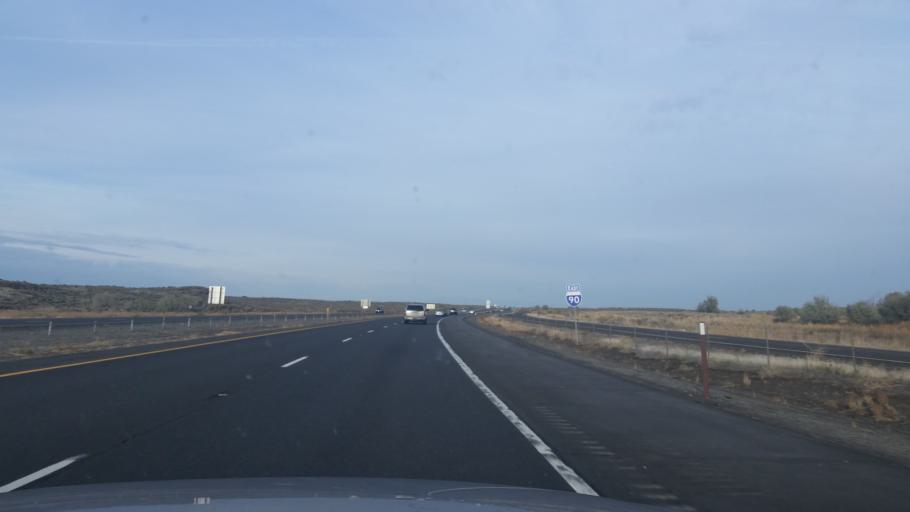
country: US
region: Washington
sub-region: Grant County
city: Quincy
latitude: 47.0268
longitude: -119.9389
